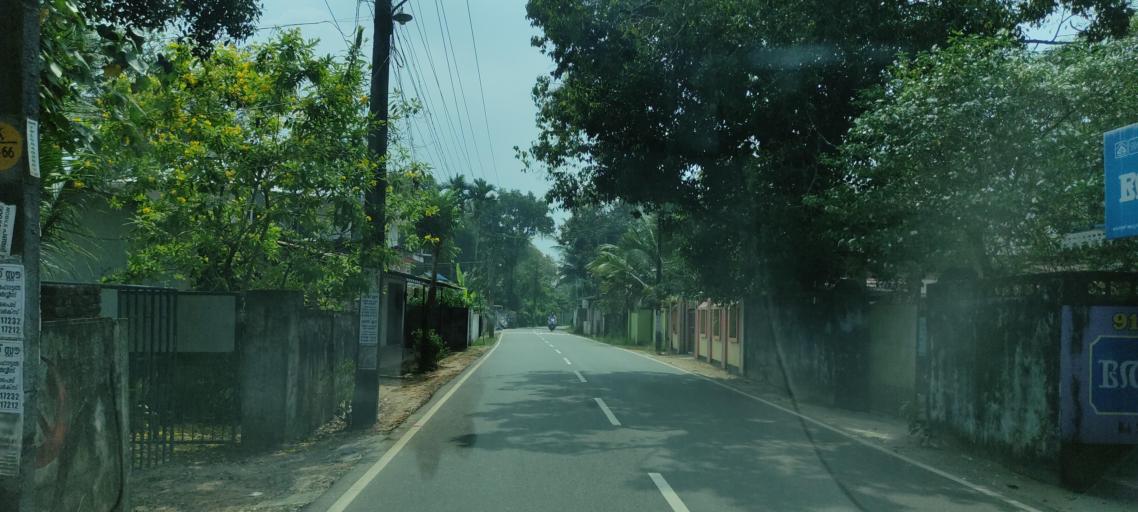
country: IN
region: Kerala
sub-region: Alappuzha
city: Alleppey
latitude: 9.5573
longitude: 76.3340
